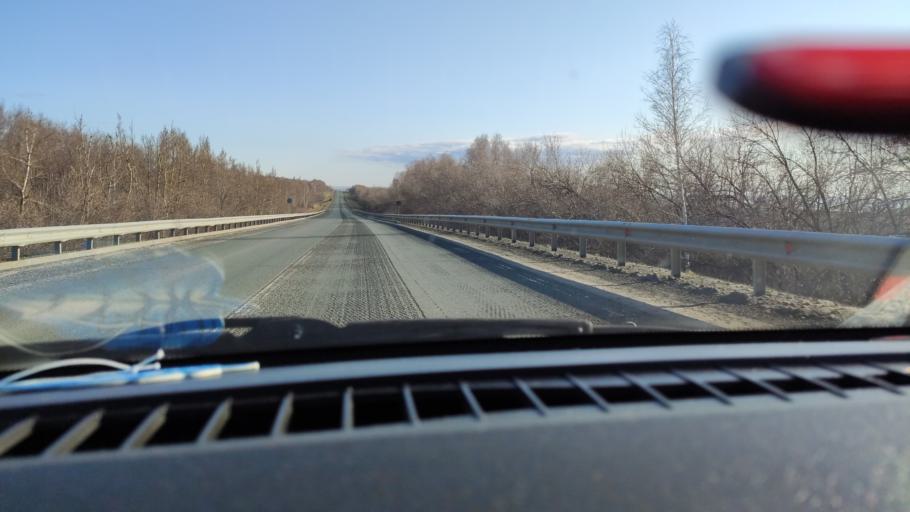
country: RU
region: Saratov
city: Dukhovnitskoye
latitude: 52.6279
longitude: 48.1816
